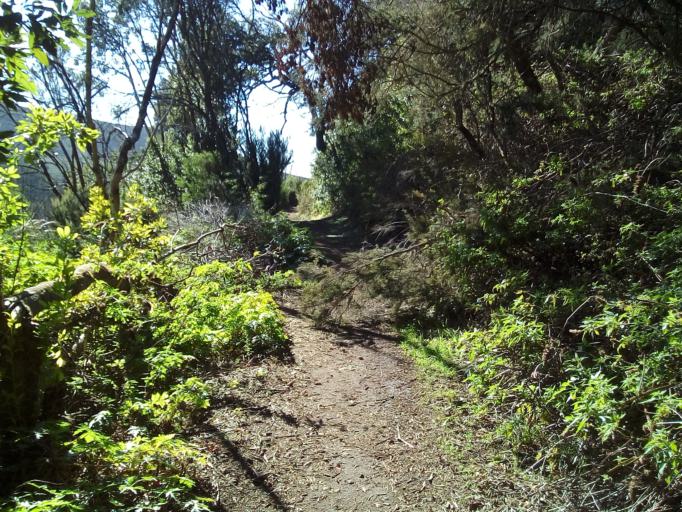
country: ES
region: Canary Islands
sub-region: Provincia de Santa Cruz de Tenerife
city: Vallehermosa
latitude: 28.1238
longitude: -17.2610
